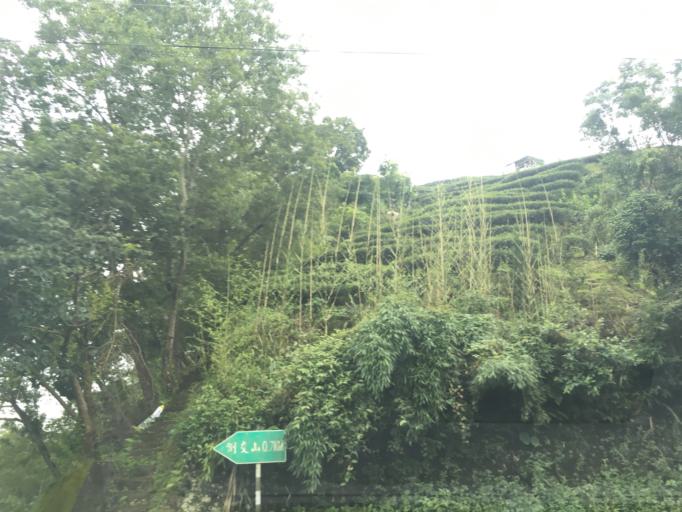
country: TW
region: Taiwan
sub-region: Yunlin
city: Douliu
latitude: 23.5647
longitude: 120.6588
